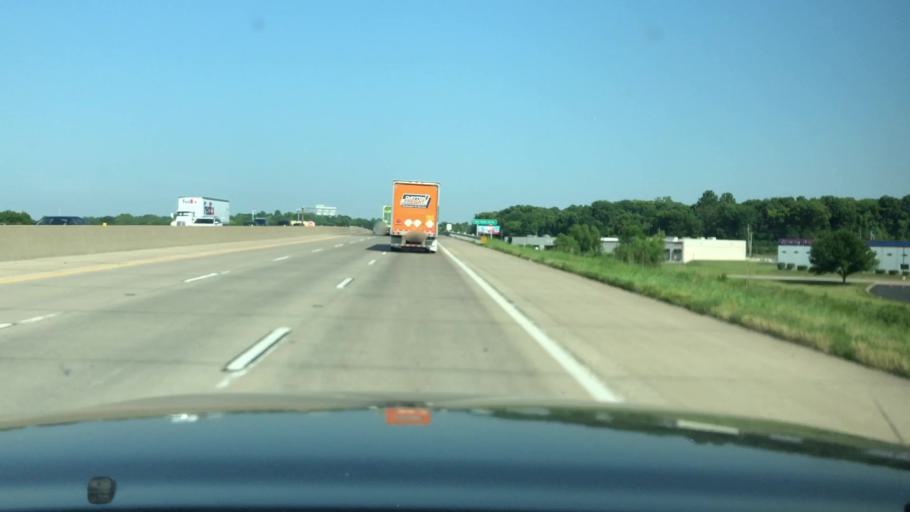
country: US
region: Missouri
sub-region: Saint Charles County
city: Saint Charles
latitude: 38.8215
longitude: -90.5087
